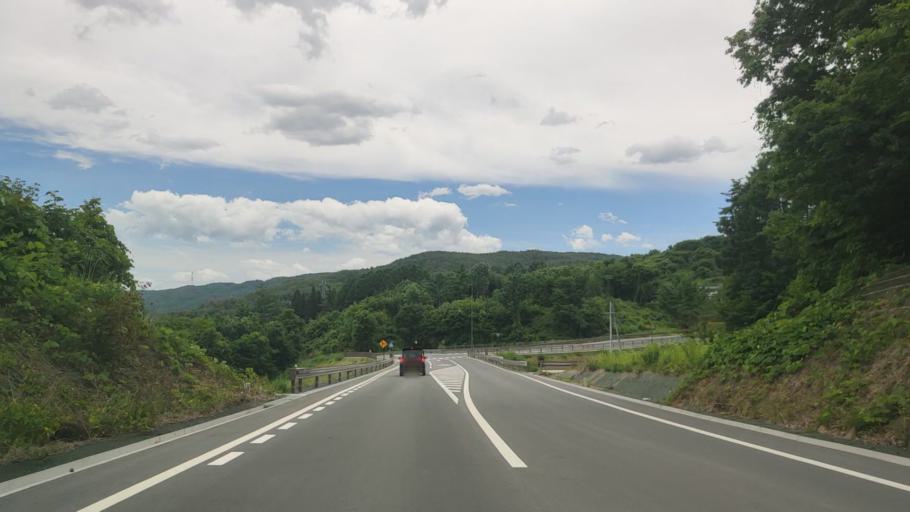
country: JP
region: Nagano
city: Kamimaruko
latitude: 36.2737
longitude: 138.3027
